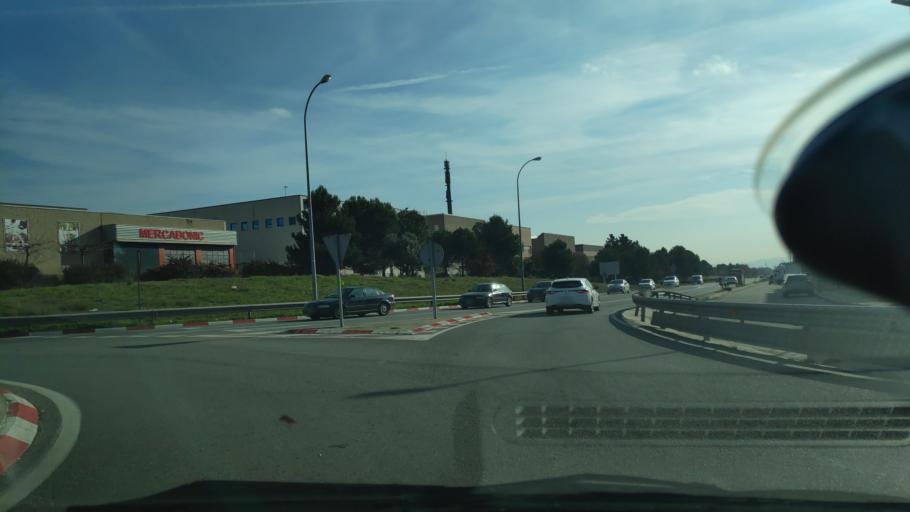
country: ES
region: Catalonia
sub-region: Provincia de Barcelona
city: Castellar del Valles
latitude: 41.6011
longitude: 2.0861
